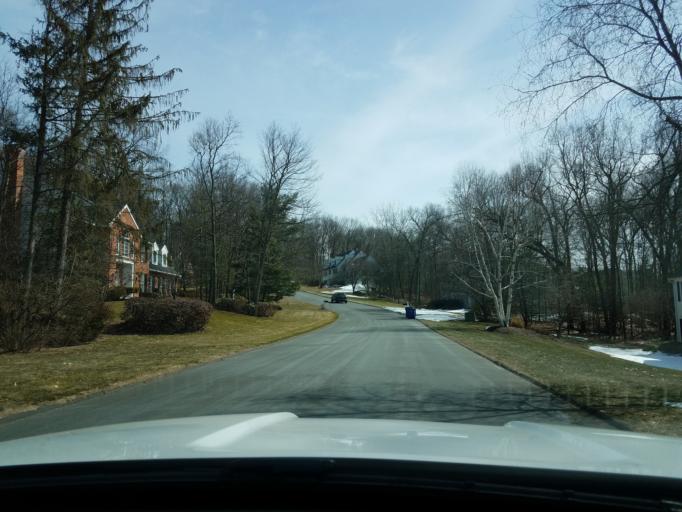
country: US
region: Connecticut
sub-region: Hartford County
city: Collinsville
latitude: 41.7863
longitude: -72.9052
